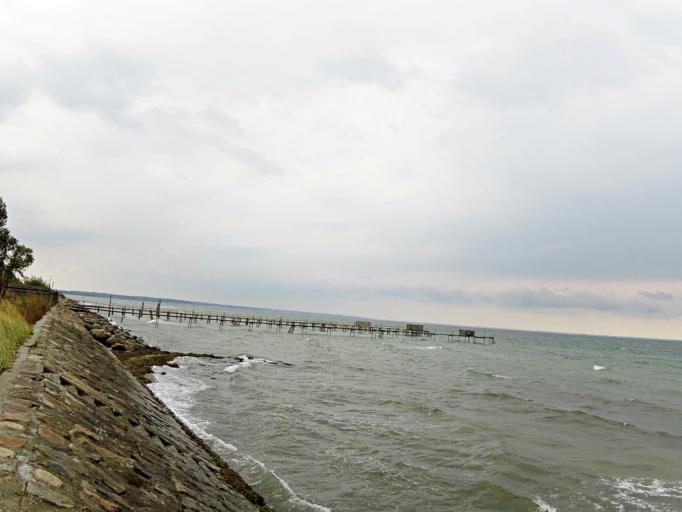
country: DK
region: Capital Region
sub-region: Horsholm Kommune
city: Horsholm
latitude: 55.8943
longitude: 12.5376
